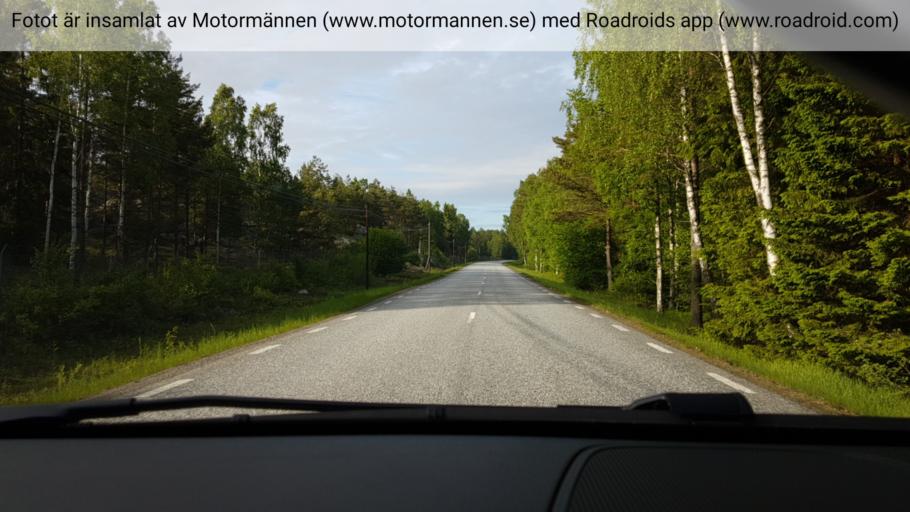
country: SE
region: Stockholm
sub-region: Nynashamns Kommun
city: Nynashamn
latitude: 58.9820
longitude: 18.0896
